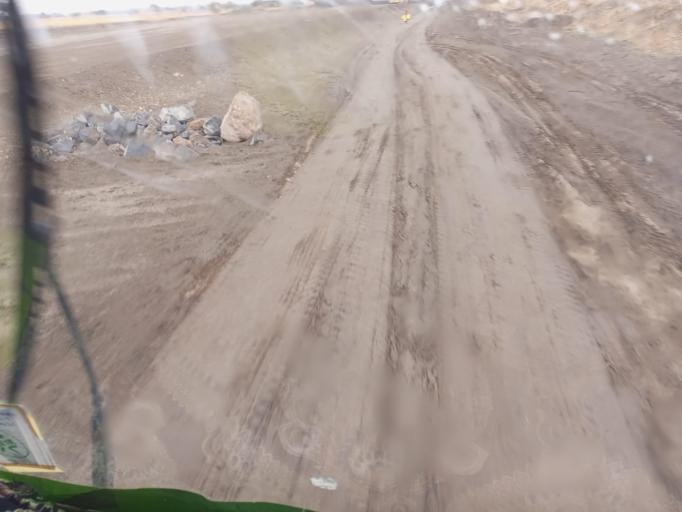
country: ET
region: Oromiya
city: Ziway
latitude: 7.7613
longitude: 38.6099
